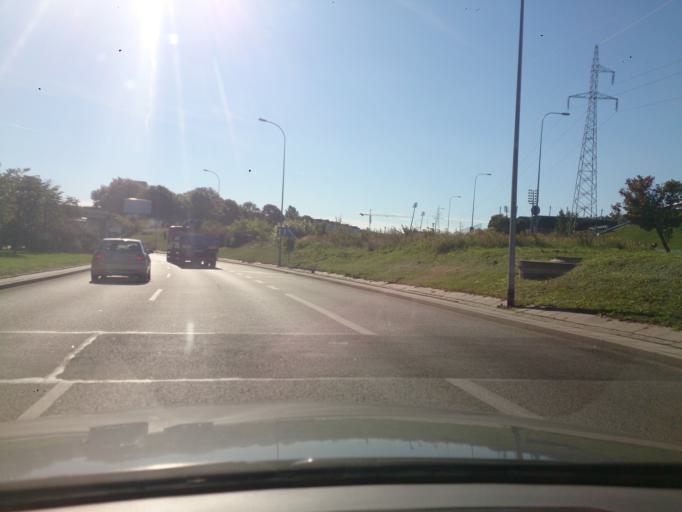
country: PL
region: Pomeranian Voivodeship
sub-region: Gdynia
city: Gdynia
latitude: 54.5012
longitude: 18.5326
